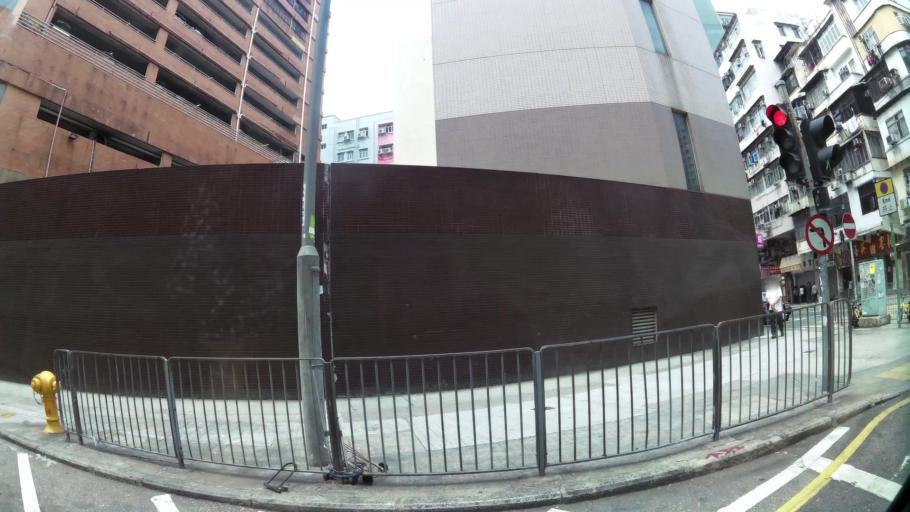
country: HK
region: Sham Shui Po
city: Sham Shui Po
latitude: 22.3394
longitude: 114.1519
